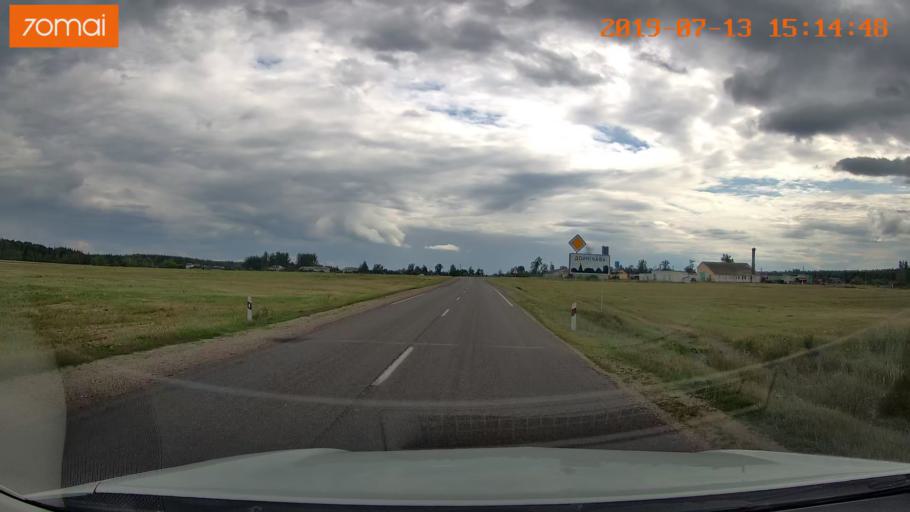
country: BY
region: Mogilev
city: Hlusha
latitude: 53.1225
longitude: 28.8215
